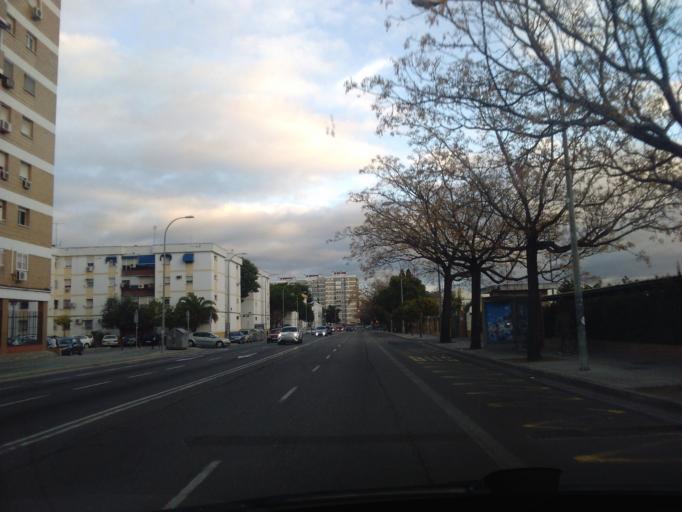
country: ES
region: Andalusia
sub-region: Provincia de Sevilla
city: Sevilla
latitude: 37.3934
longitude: -5.9622
